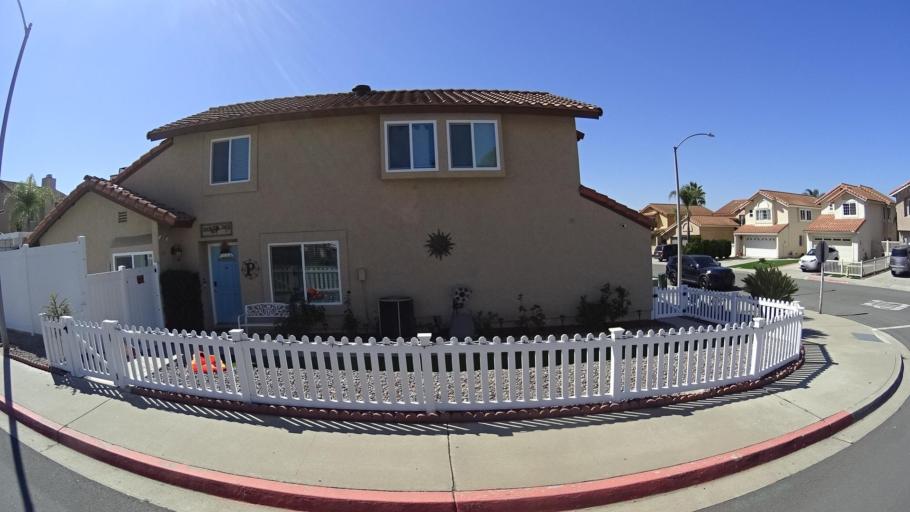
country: US
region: California
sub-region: San Diego County
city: Rancho San Diego
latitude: 32.7448
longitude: -116.9253
